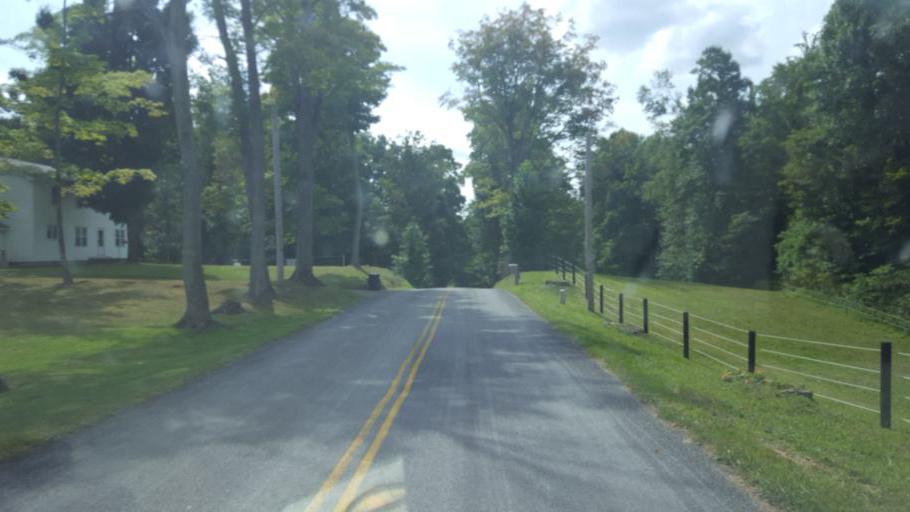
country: US
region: Ohio
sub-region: Geauga County
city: Middlefield
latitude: 41.4329
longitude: -80.9731
